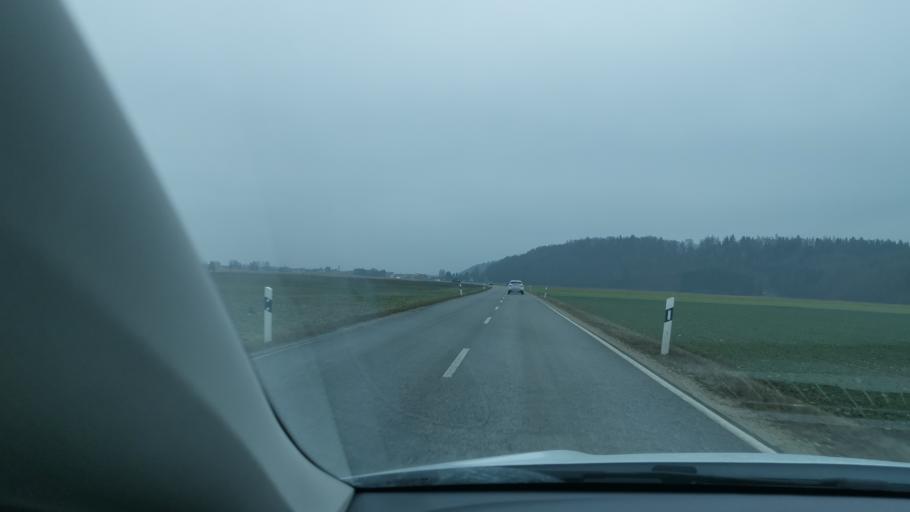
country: DE
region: Bavaria
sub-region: Swabia
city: Todtenweis
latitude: 48.5032
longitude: 10.9205
